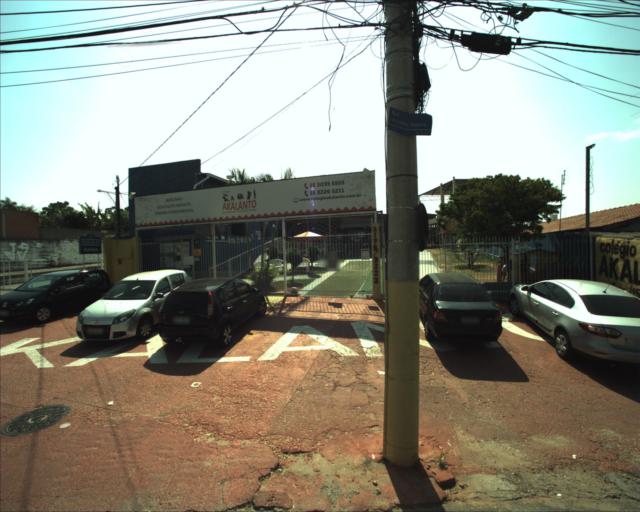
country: BR
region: Sao Paulo
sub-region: Sorocaba
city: Sorocaba
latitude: -23.4596
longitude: -47.4825
